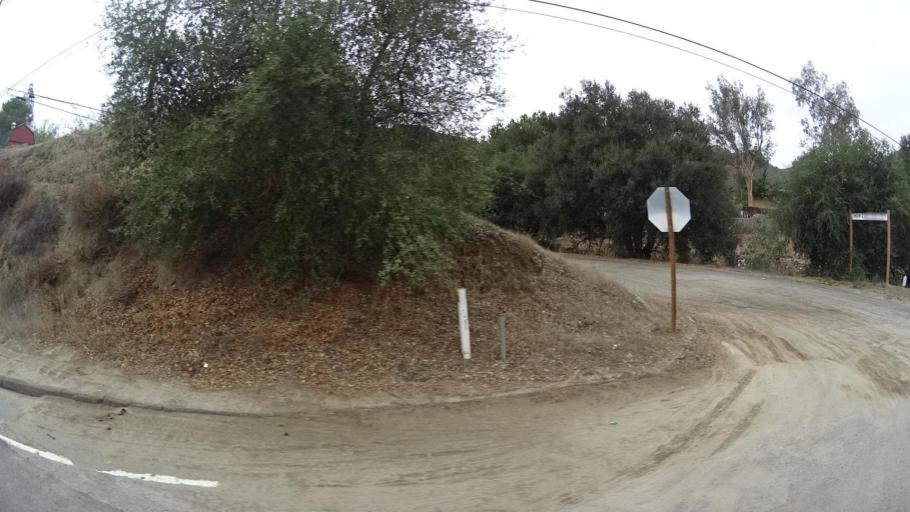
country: US
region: California
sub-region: San Diego County
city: Ramona
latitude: 33.0744
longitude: -116.9028
